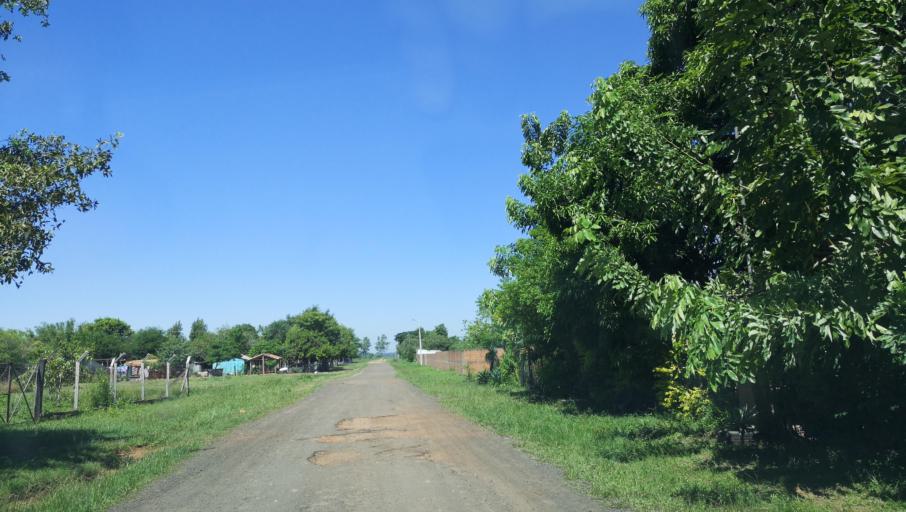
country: PY
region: Caaguazu
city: Carayao
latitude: -25.1935
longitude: -56.4053
